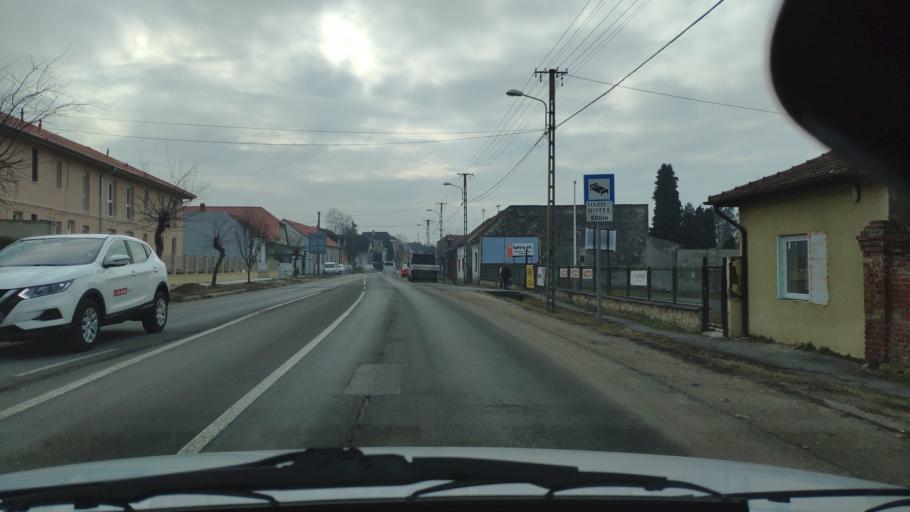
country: HU
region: Zala
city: Nagykanizsa
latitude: 46.4657
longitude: 16.9859
